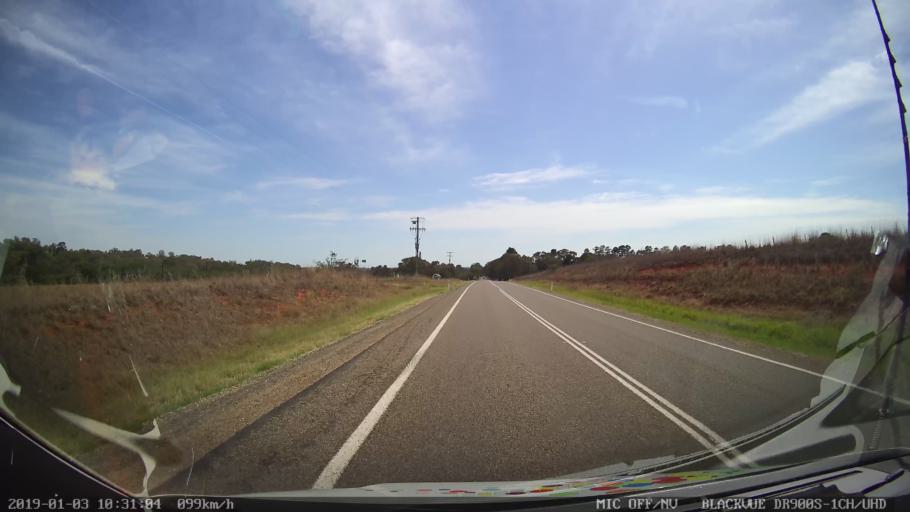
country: AU
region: New South Wales
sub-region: Young
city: Young
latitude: -34.3545
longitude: 148.2737
